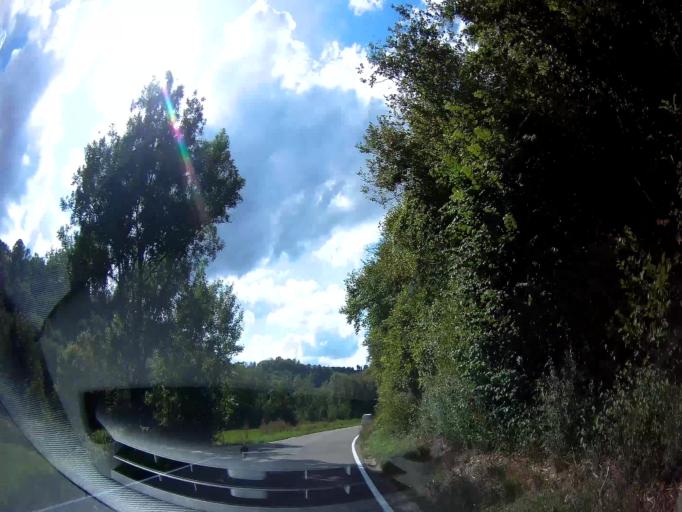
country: BE
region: Wallonia
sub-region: Province de Namur
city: Anhee
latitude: 50.3037
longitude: 4.8271
